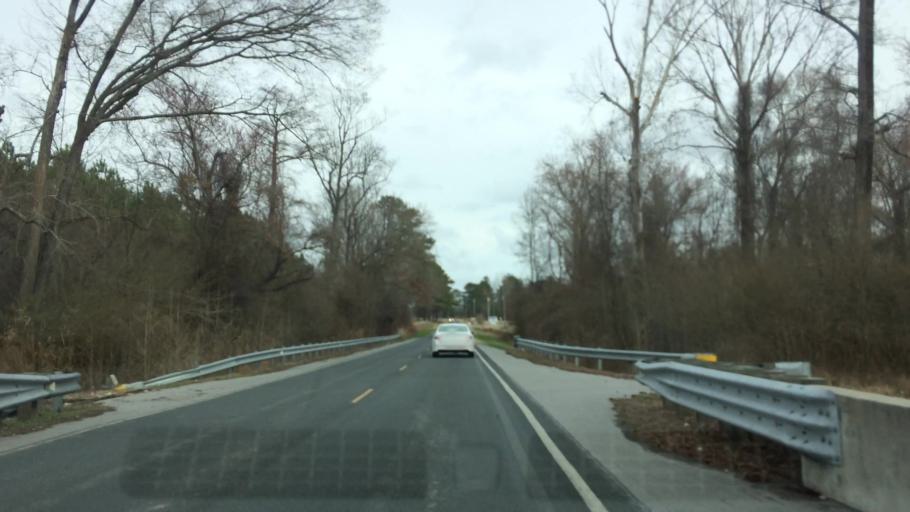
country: US
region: North Carolina
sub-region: Pitt County
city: Ayden
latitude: 35.4889
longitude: -77.3662
